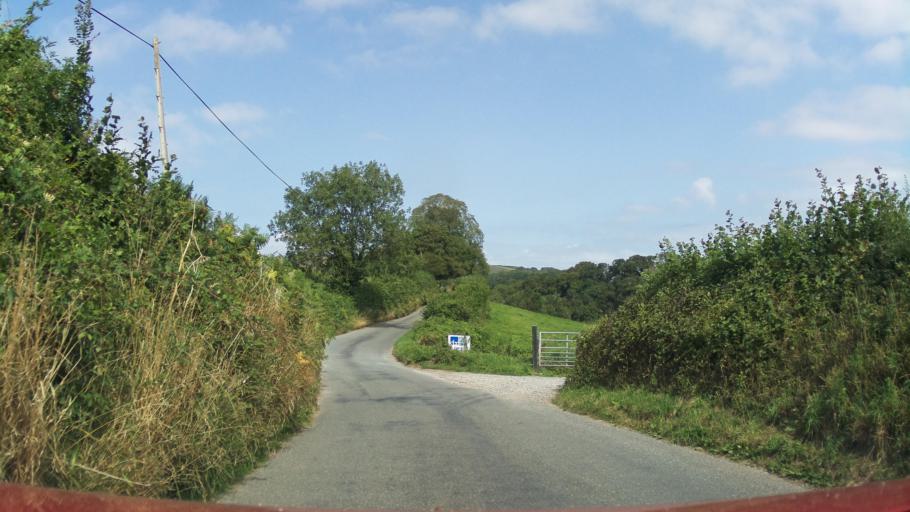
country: GB
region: England
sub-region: Borough of Torbay
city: Paignton
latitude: 50.4033
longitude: -3.6068
